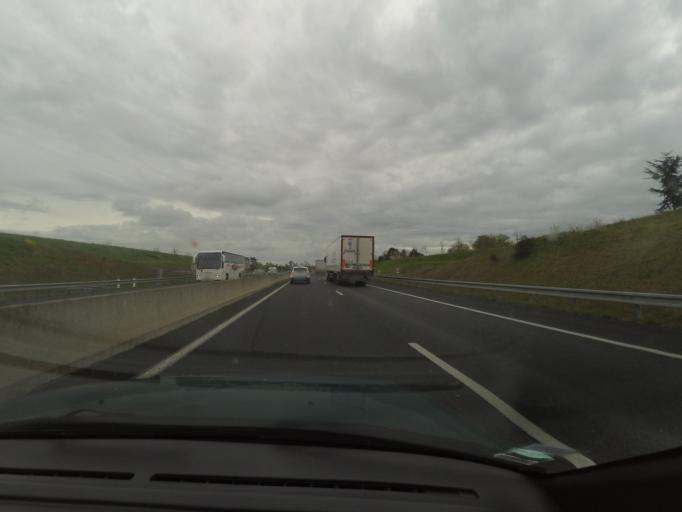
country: FR
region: Pays de la Loire
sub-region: Departement de Maine-et-Loire
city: Avrille
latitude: 47.4962
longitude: -0.5629
